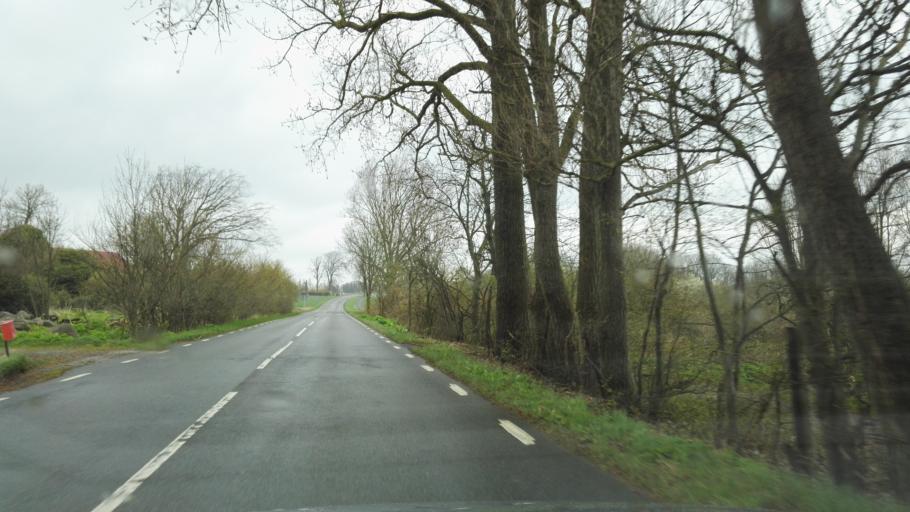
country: SE
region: Skane
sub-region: Simrishamns Kommun
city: Simrishamn
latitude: 55.4992
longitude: 14.3203
